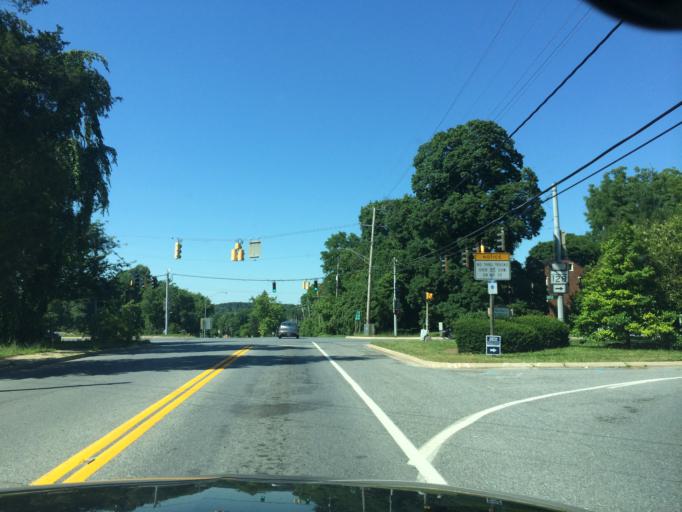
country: US
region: Maryland
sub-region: Baltimore County
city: Reisterstown
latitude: 39.4750
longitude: -76.8291
